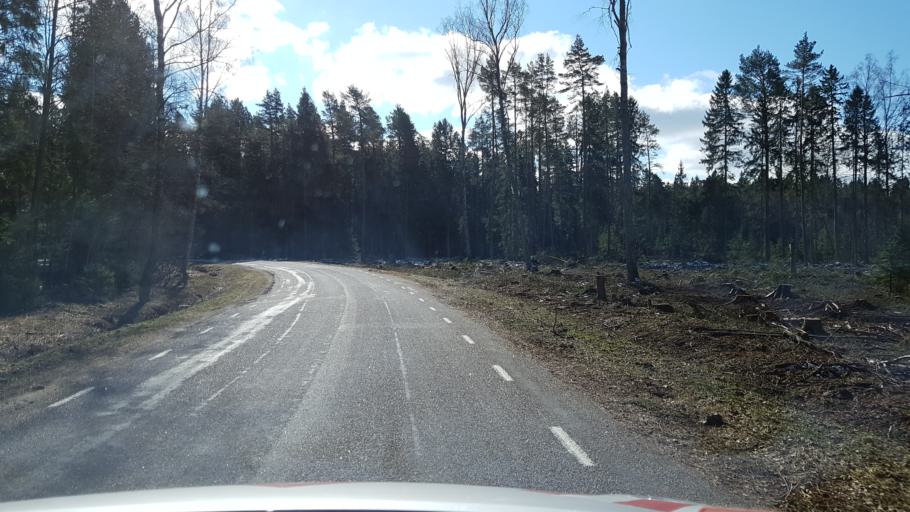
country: EE
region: Harju
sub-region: Loksa linn
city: Loksa
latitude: 59.5787
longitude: 25.9188
